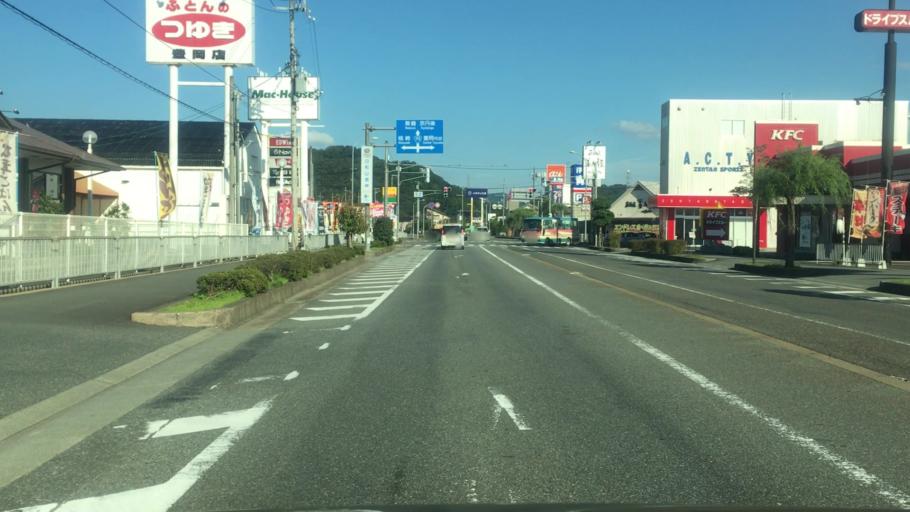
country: JP
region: Hyogo
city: Toyooka
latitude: 35.5542
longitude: 134.8145
